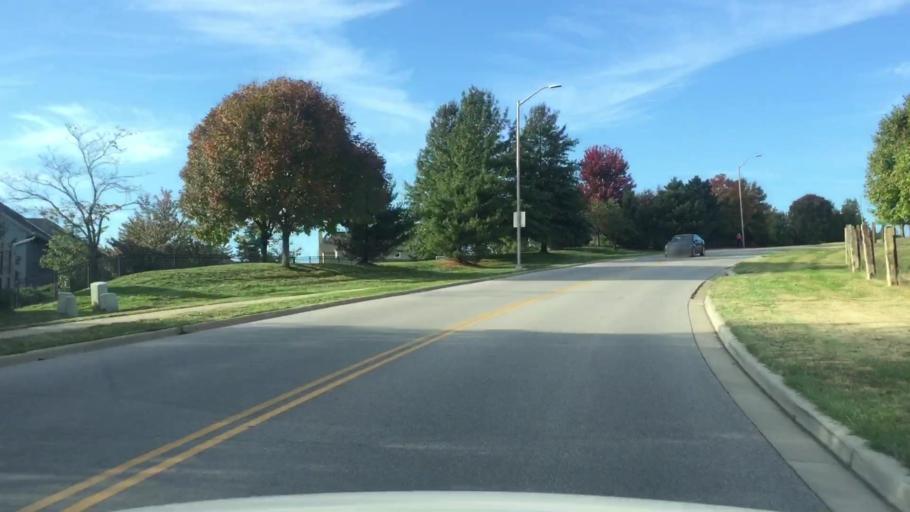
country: US
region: Kansas
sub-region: Johnson County
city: Shawnee
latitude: 39.0330
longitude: -94.7495
